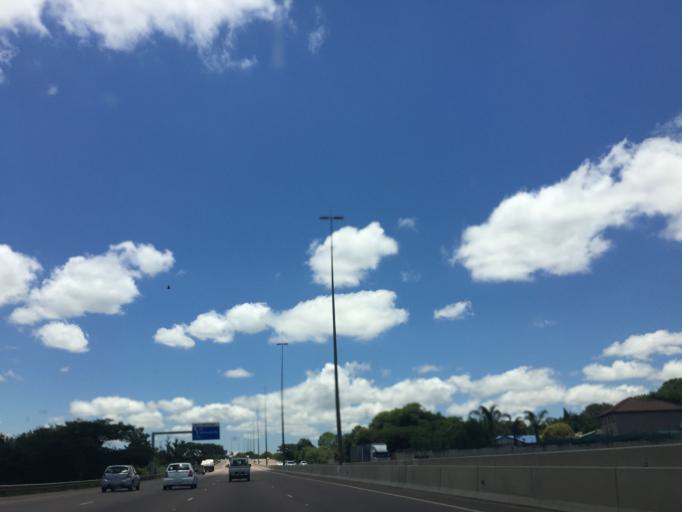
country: ZA
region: Gauteng
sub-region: City of Tshwane Metropolitan Municipality
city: Pretoria
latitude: -25.7008
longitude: 28.2765
